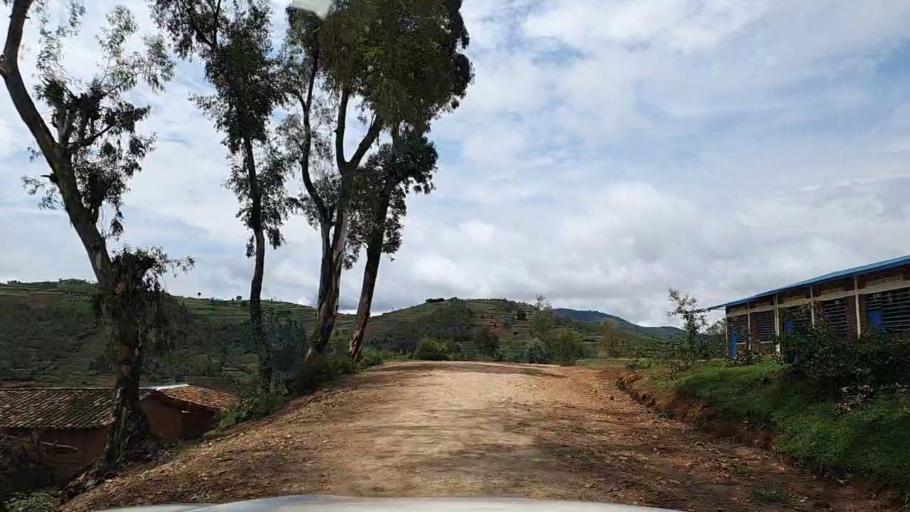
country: RW
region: Southern Province
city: Gikongoro
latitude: -2.3363
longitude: 29.5208
